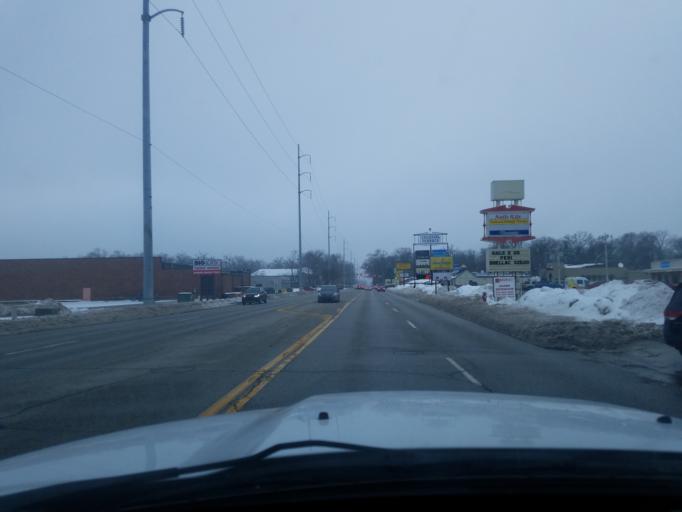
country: US
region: Indiana
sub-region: Saint Joseph County
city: Mishawaka
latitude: 41.6823
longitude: -86.1966
